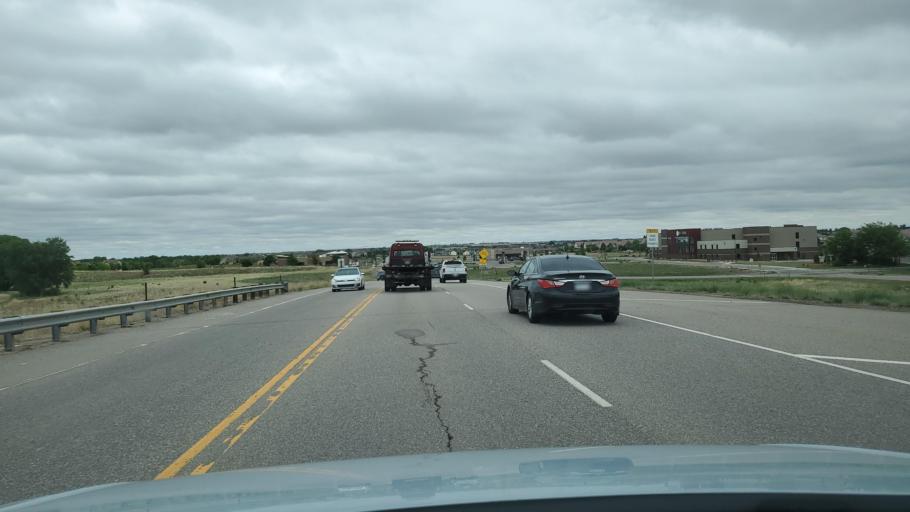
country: US
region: Colorado
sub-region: Adams County
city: Brighton
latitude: 39.9143
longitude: -104.8134
